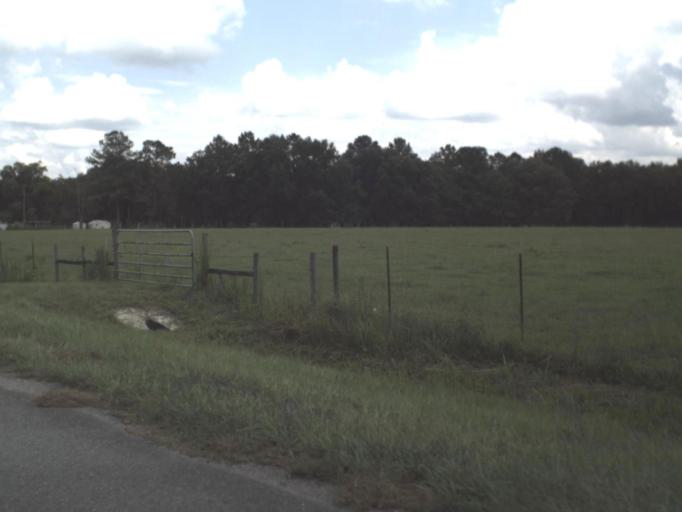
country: US
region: Florida
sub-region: Union County
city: Lake Butler
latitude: 30.0533
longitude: -82.2582
